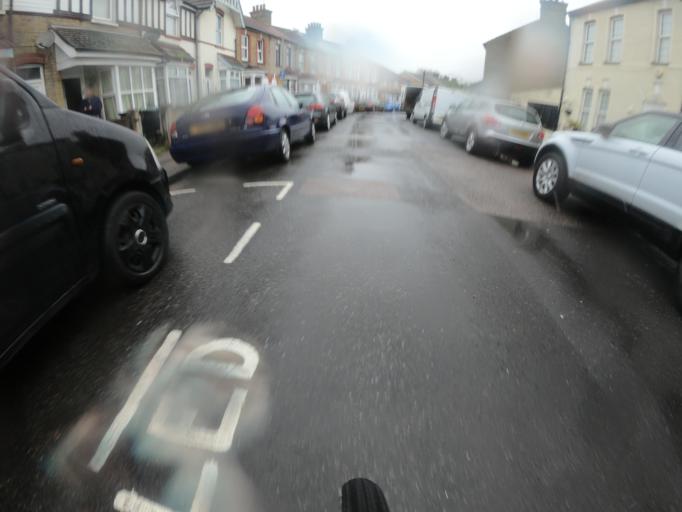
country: GB
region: England
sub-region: Kent
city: Gravesend
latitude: 51.4347
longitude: 0.3513
